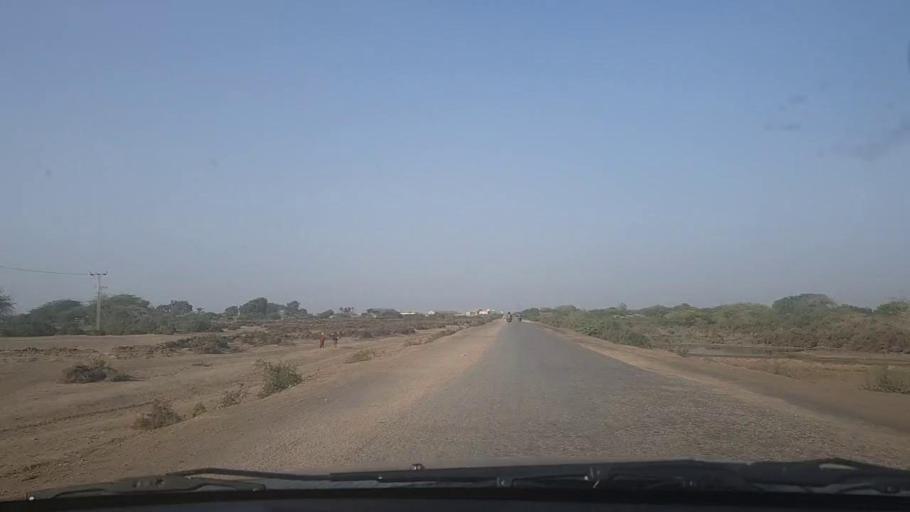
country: PK
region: Sindh
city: Keti Bandar
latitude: 24.3082
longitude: 67.6074
